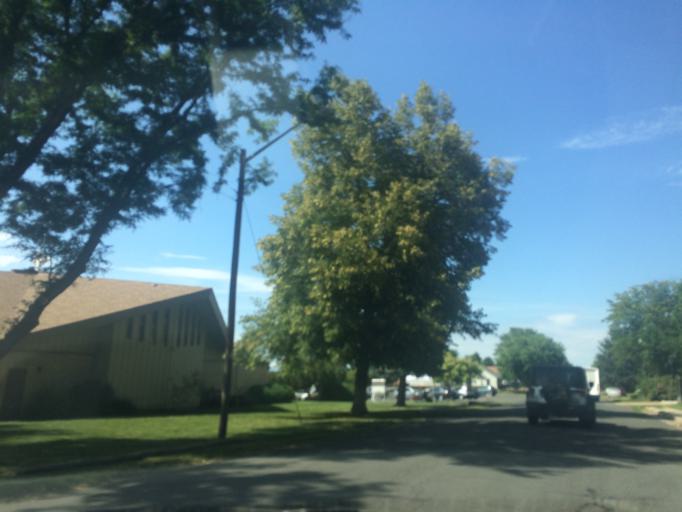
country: US
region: Colorado
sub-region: Jefferson County
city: Wheat Ridge
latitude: 39.7767
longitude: -105.0890
